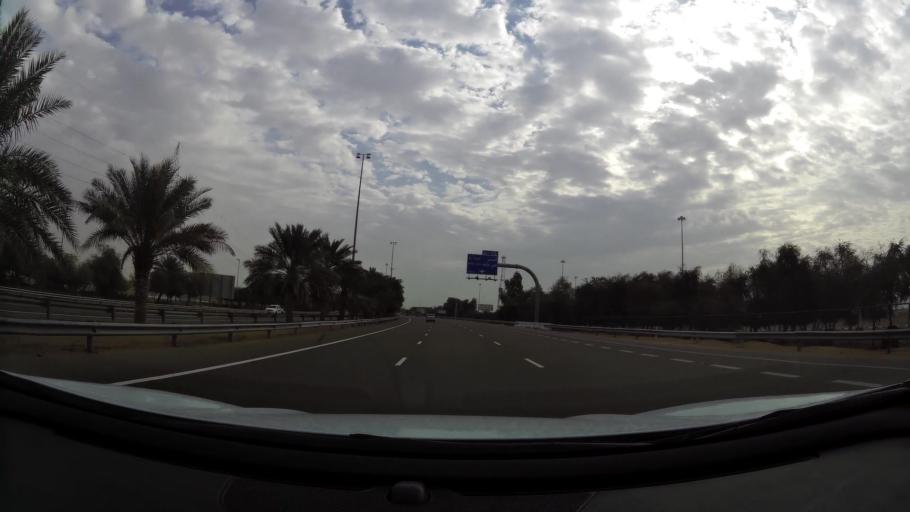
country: AE
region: Abu Dhabi
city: Al Ain
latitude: 24.2099
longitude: 55.5139
